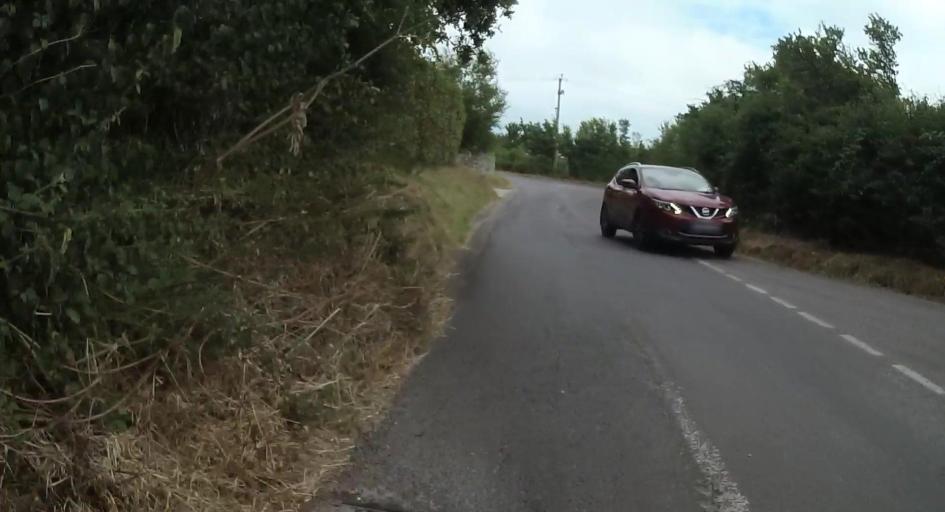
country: GB
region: England
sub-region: Dorset
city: Swanage
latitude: 50.6228
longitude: -1.9672
